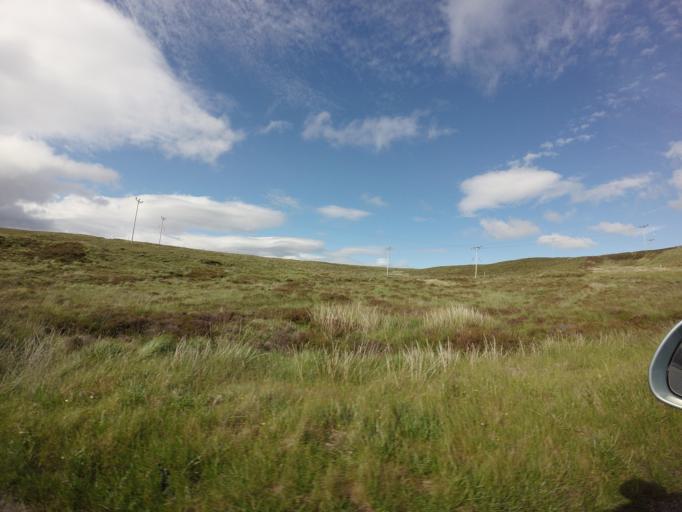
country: GB
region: Scotland
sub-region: Eilean Siar
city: Stornoway
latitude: 58.1762
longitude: -6.6166
